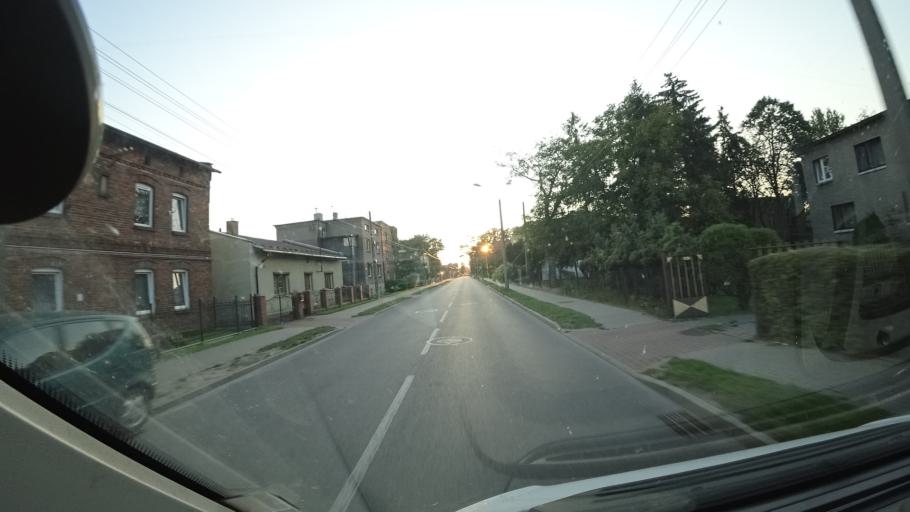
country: PL
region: Silesian Voivodeship
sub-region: Zabrze
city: Zabrze
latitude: 50.2808
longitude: 18.8104
